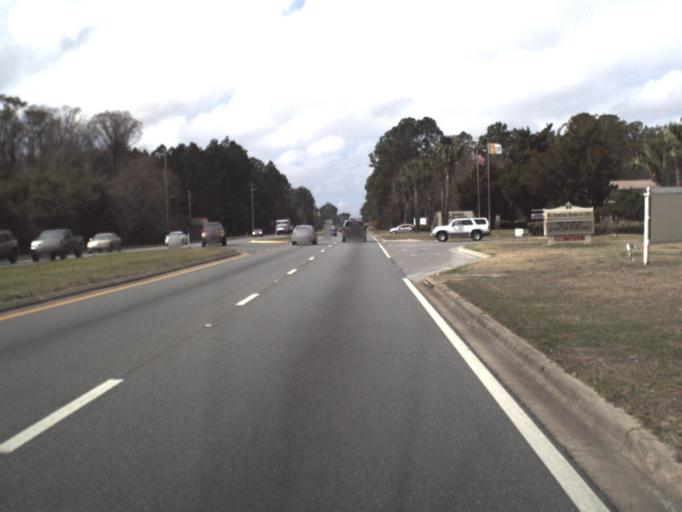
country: US
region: Florida
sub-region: Bay County
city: Cedar Grove
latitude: 30.1750
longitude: -85.6120
